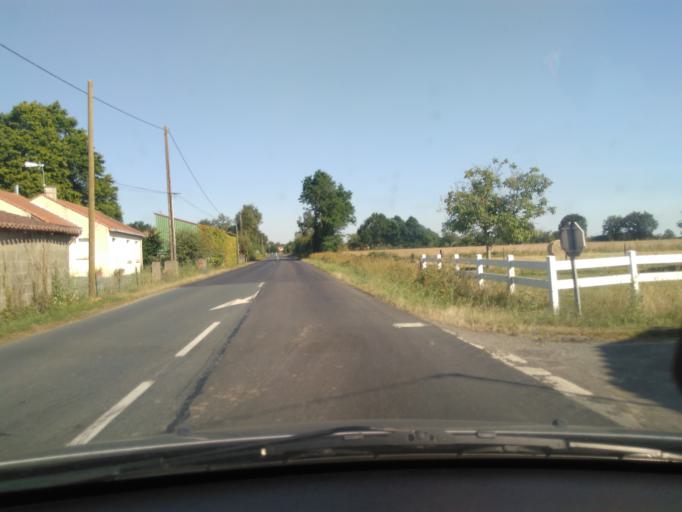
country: FR
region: Pays de la Loire
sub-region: Departement de la Vendee
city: Dompierre-sur-Yon
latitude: 46.7258
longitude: -1.3545
